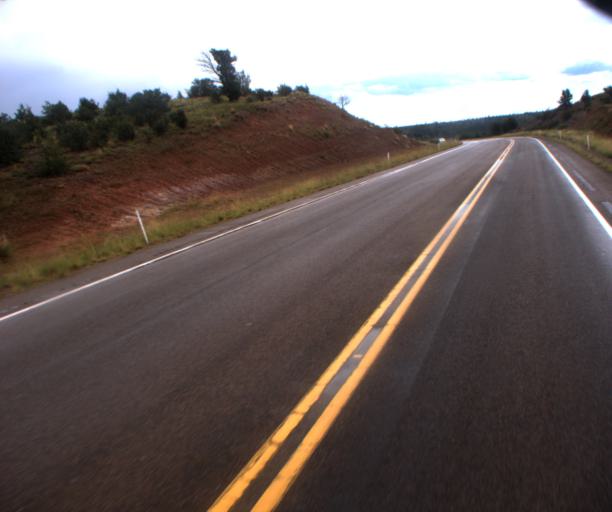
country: US
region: Arizona
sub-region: Navajo County
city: Heber-Overgaard
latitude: 34.3667
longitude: -110.4221
